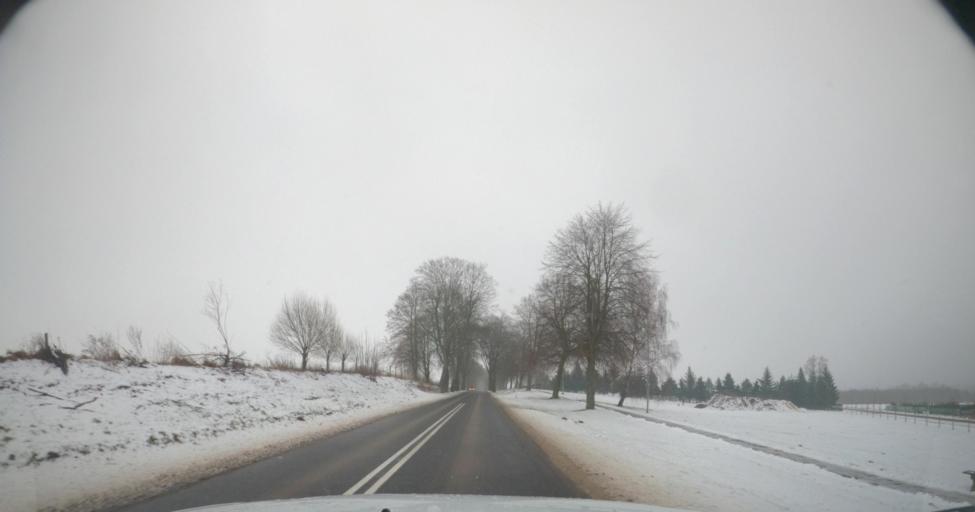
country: PL
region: West Pomeranian Voivodeship
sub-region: Powiat gryficki
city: Gryfice
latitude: 53.9110
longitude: 15.2246
